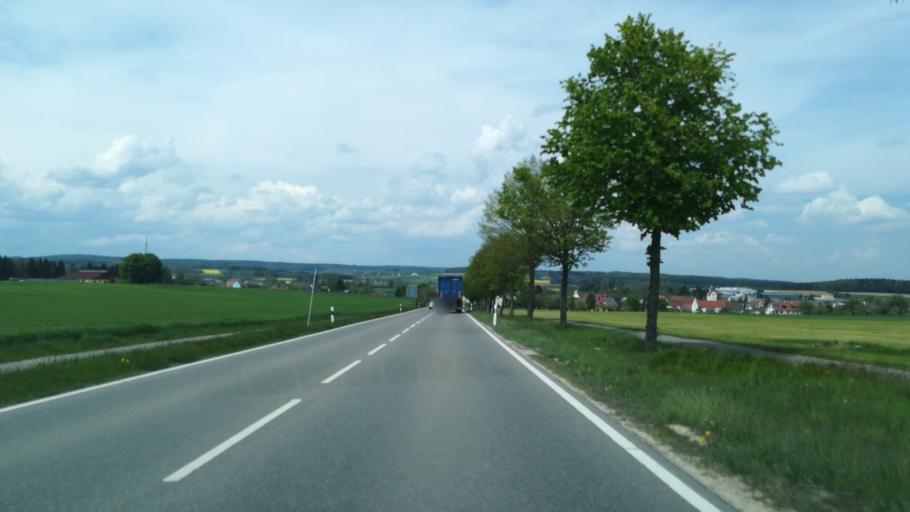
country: DE
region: Baden-Wuerttemberg
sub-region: Freiburg Region
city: Muhlingen
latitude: 47.9551
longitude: 9.0446
